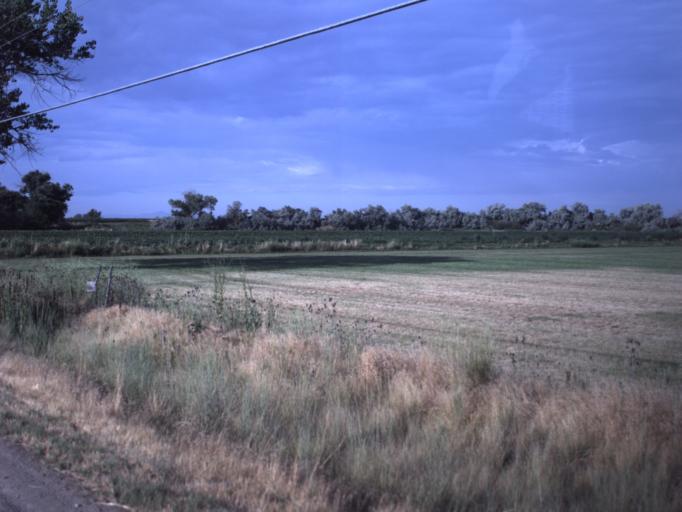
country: US
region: Utah
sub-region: Weber County
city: Plain City
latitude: 41.2704
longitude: -112.0924
